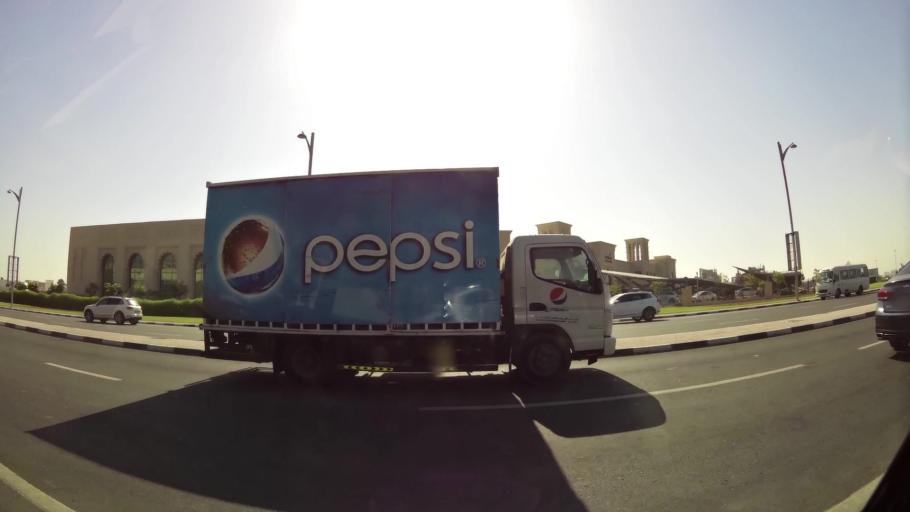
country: AE
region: Dubai
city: Dubai
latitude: 25.1335
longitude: 55.1882
